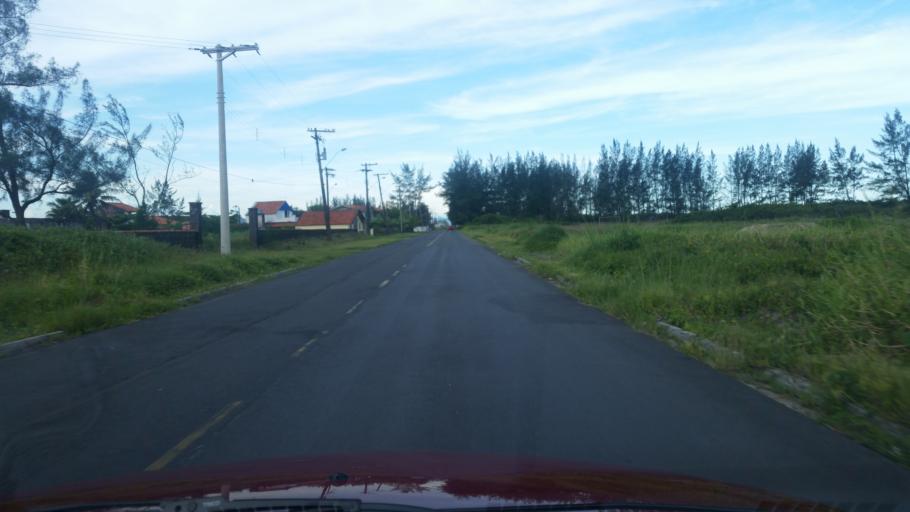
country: BR
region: Sao Paulo
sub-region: Iguape
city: Iguape
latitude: -24.8004
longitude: -47.6291
